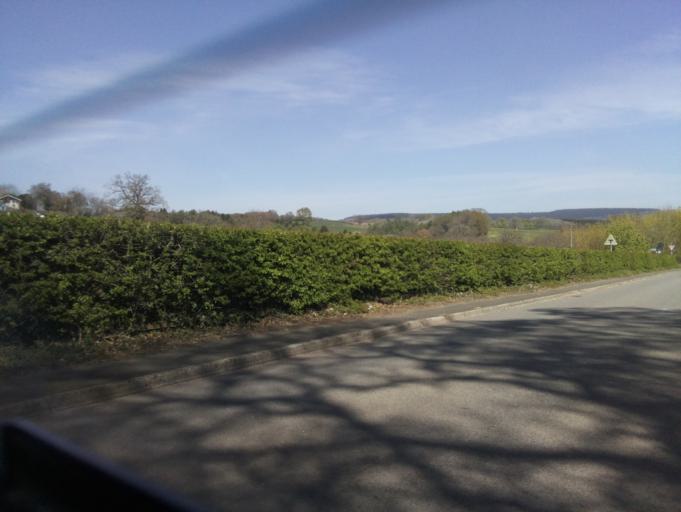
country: GB
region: Wales
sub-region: Monmouthshire
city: Caldicot
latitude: 51.6435
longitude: -2.7456
